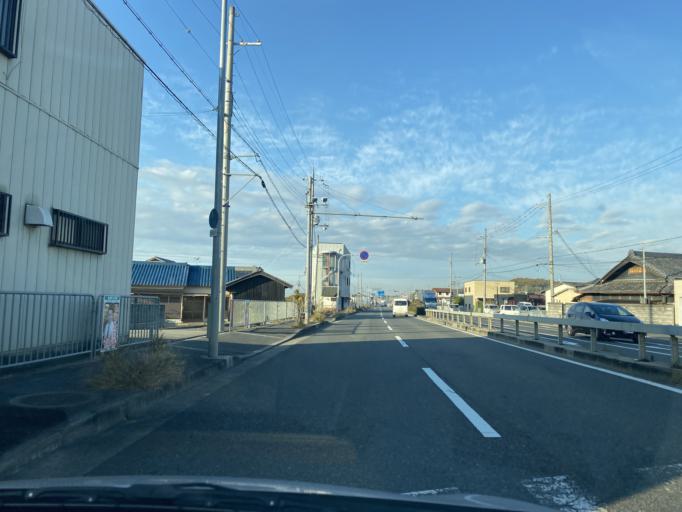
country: JP
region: Osaka
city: Izumi
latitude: 34.4301
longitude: 135.4399
